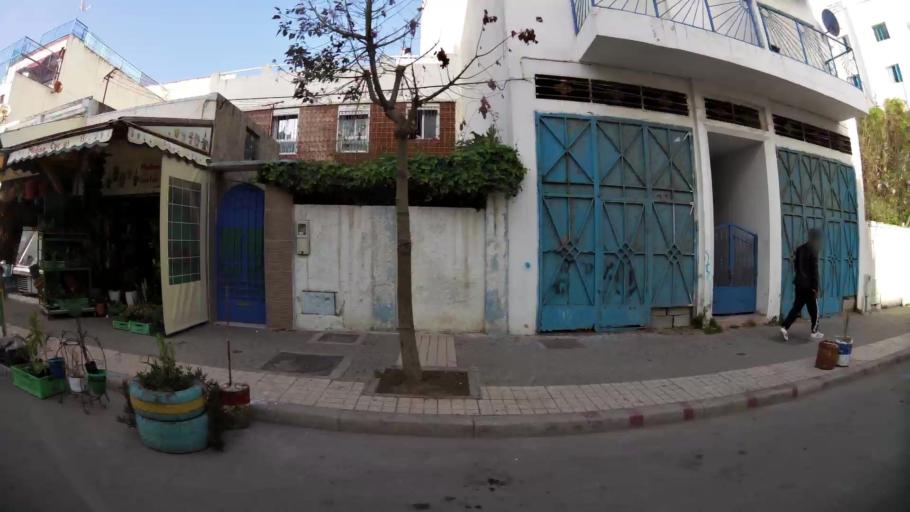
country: MA
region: Tanger-Tetouan
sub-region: Tetouan
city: Martil
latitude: 35.6165
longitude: -5.2721
